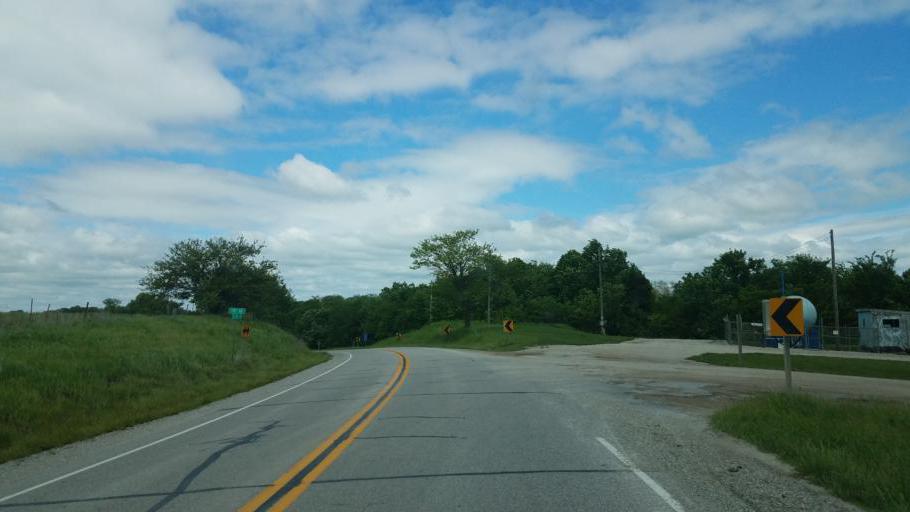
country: US
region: Iowa
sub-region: Decatur County
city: Lamoni
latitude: 40.6238
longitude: -93.8449
